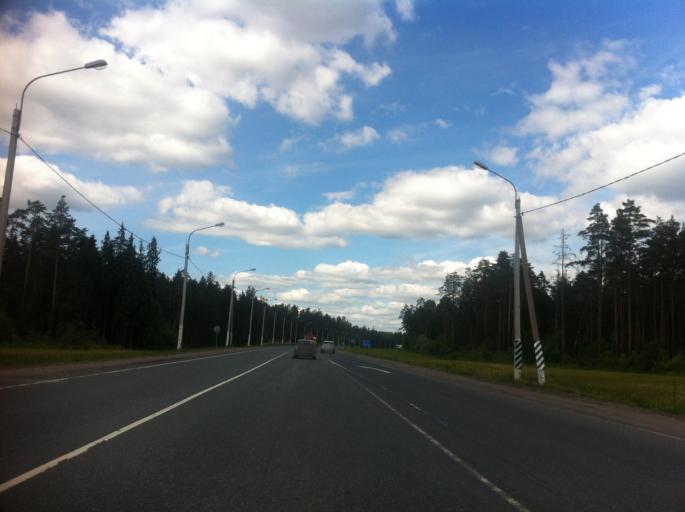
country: RU
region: Leningrad
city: Luga
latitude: 58.7166
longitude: 29.8782
